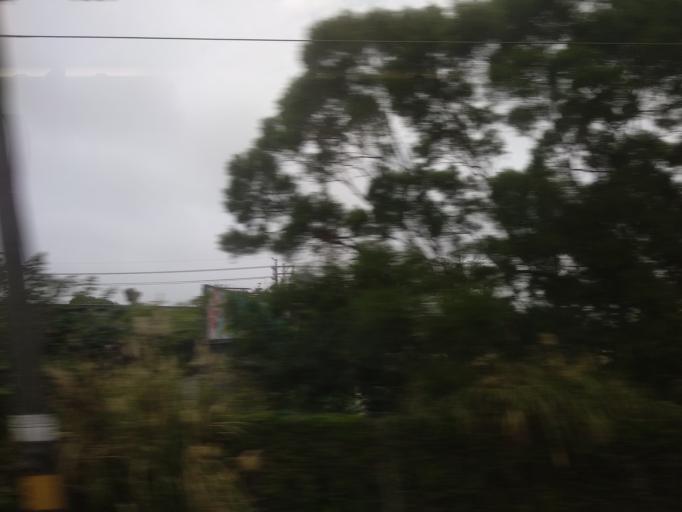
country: TW
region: Taiwan
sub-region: Hsinchu
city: Zhubei
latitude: 24.8906
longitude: 121.0247
